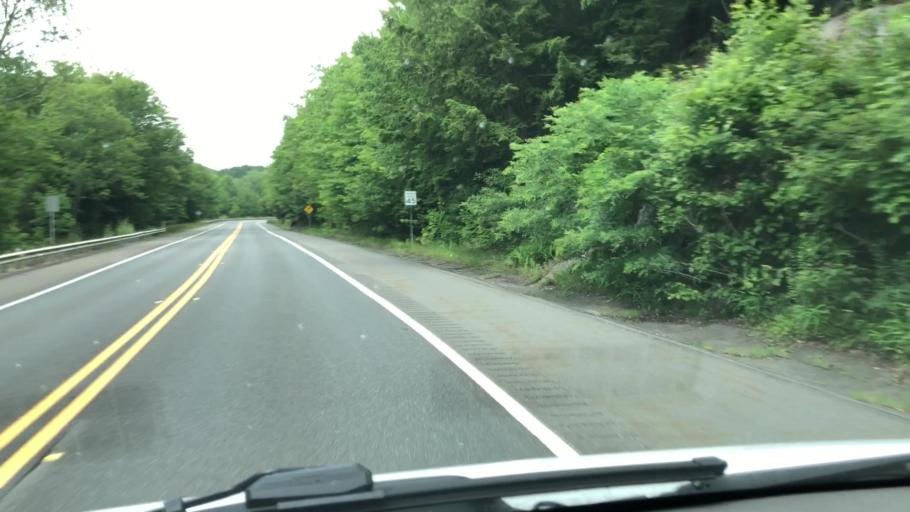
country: US
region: Massachusetts
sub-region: Hampshire County
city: Chesterfield
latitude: 42.4504
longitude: -72.8555
